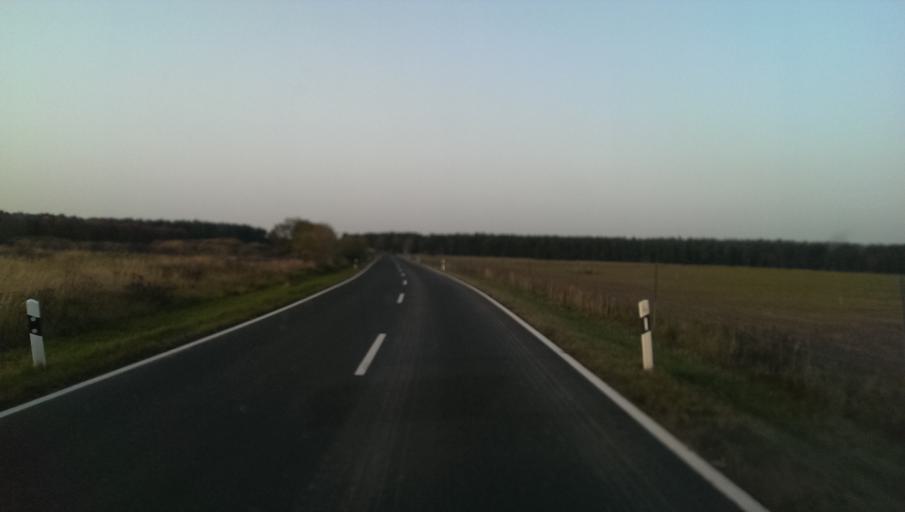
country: DE
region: Brandenburg
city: Niedergorsdorf
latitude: 51.8981
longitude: 13.0242
